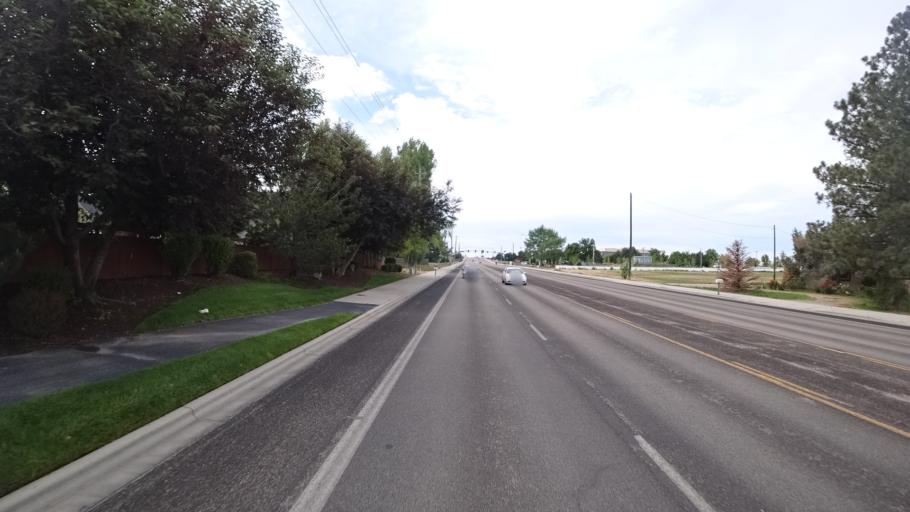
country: US
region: Idaho
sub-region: Ada County
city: Meridian
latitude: 43.5979
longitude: -116.3745
